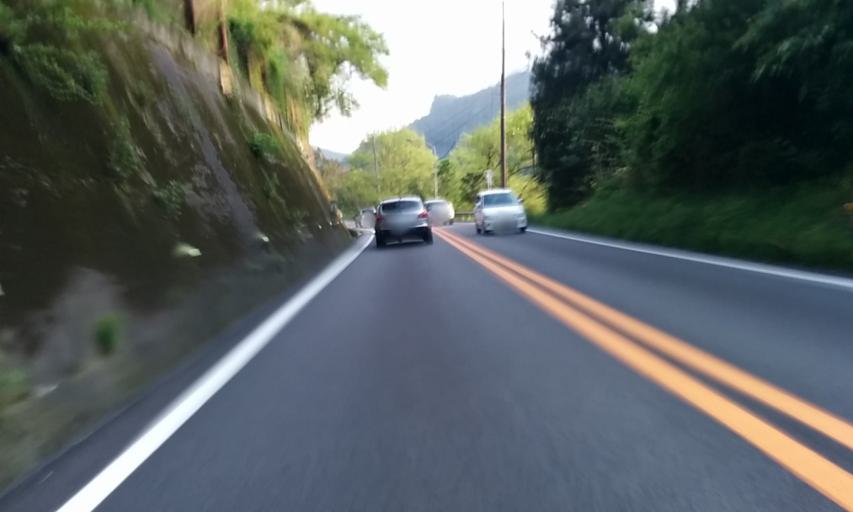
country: JP
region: Ehime
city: Saijo
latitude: 33.8380
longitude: 132.9912
